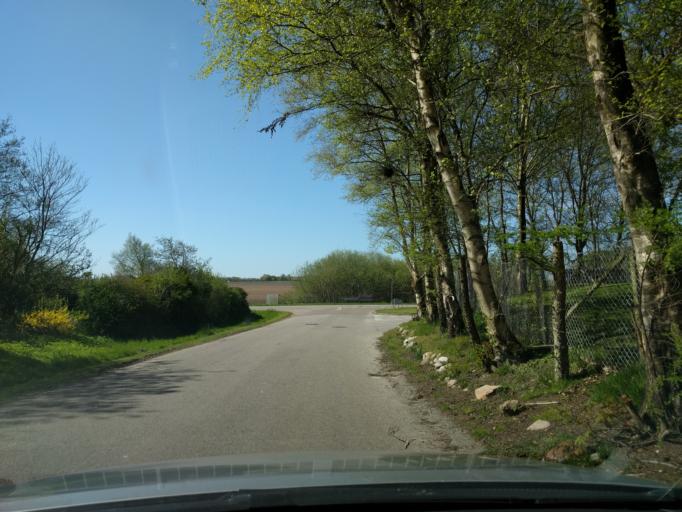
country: DK
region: South Denmark
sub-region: Varde Kommune
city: Olgod
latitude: 55.7831
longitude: 8.6560
